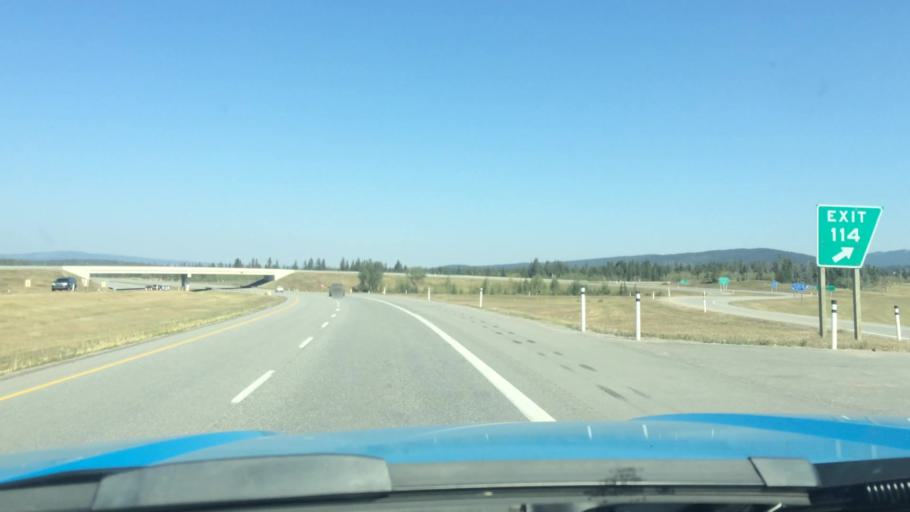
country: CA
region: Alberta
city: Canmore
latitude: 51.0758
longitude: -115.0606
